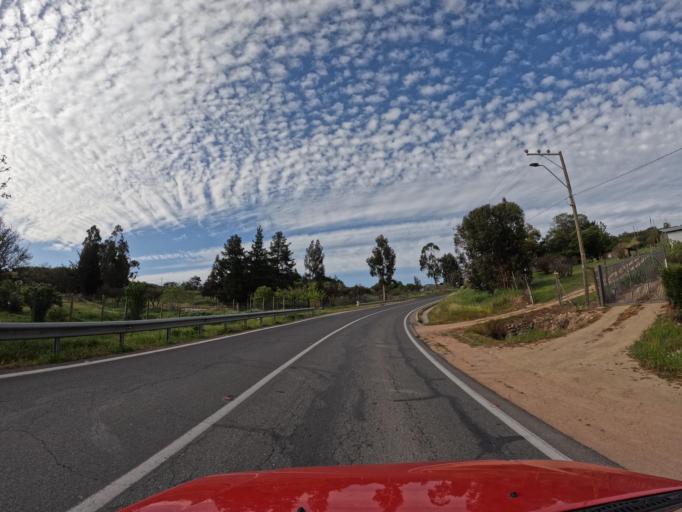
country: CL
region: O'Higgins
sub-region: Provincia de Colchagua
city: Santa Cruz
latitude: -34.2640
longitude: -71.7330
